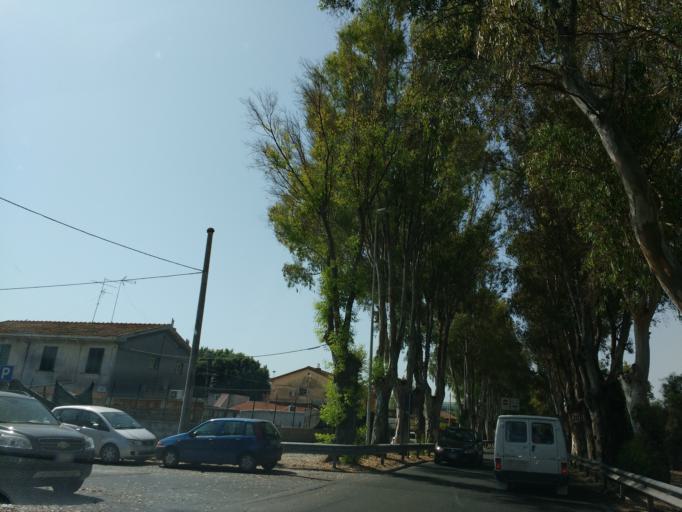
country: IT
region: Sicily
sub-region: Catania
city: Catania
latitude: 37.4736
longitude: 15.0660
